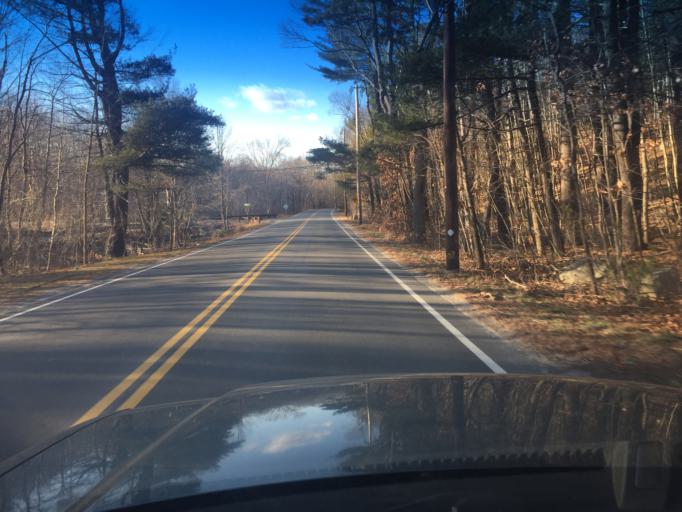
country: US
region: Massachusetts
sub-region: Middlesex County
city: Sherborn
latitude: 42.2590
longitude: -71.3738
